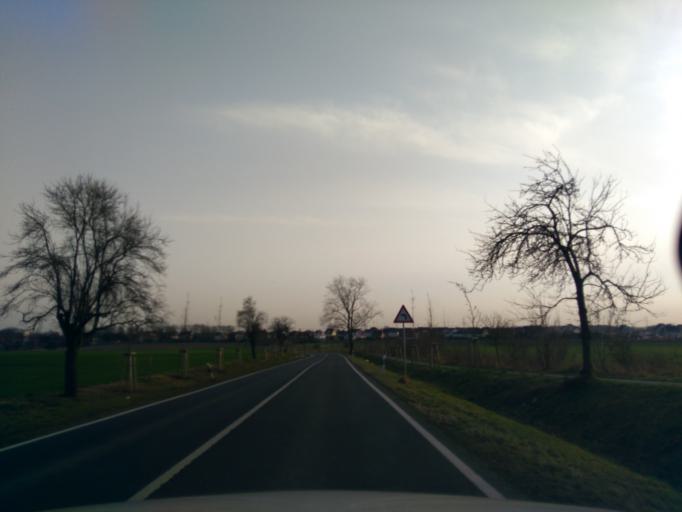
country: DE
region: Brandenburg
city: Velten
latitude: 52.6803
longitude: 13.1293
